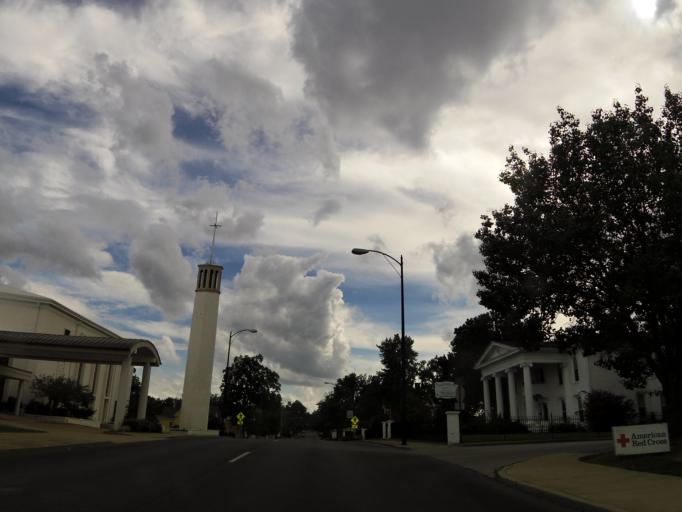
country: US
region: Kentucky
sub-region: Christian County
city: Hopkinsville
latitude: 36.8627
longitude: -87.4909
